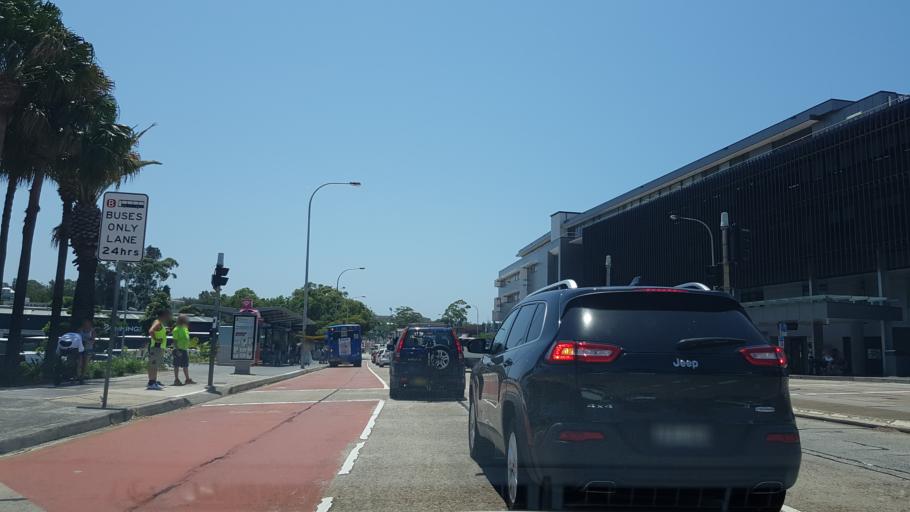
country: AU
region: New South Wales
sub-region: Warringah
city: North Manly
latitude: -33.7680
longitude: 151.2680
